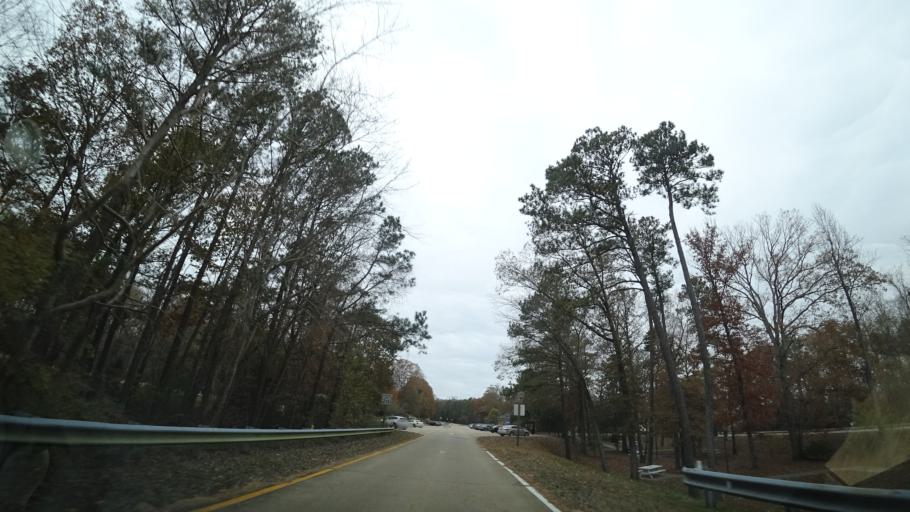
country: US
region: Virginia
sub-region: New Kent County
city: New Kent
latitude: 37.4987
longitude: -77.0423
